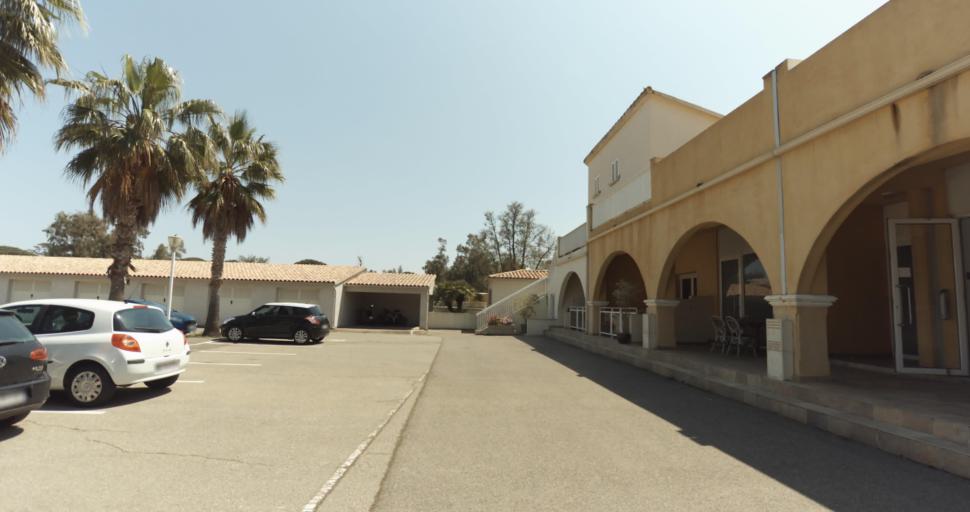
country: FR
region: Corsica
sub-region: Departement de la Haute-Corse
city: Biguglia
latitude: 42.6155
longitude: 9.4791
